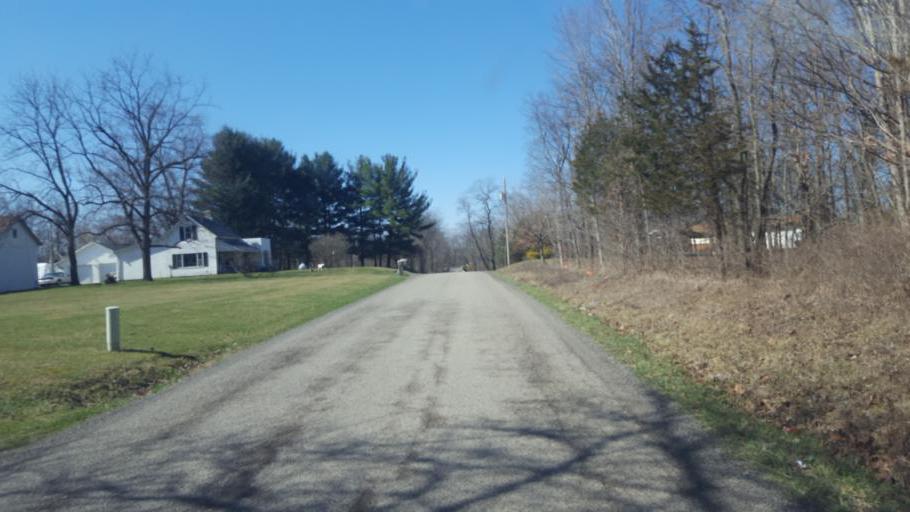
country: US
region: Ohio
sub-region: Morrow County
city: Cardington
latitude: 40.4991
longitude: -82.9109
